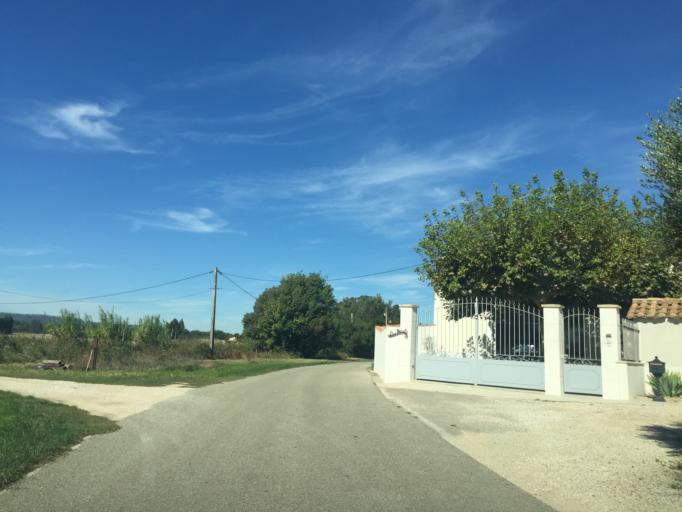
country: FR
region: Provence-Alpes-Cote d'Azur
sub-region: Departement du Vaucluse
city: Caderousse
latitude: 44.1003
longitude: 4.7468
